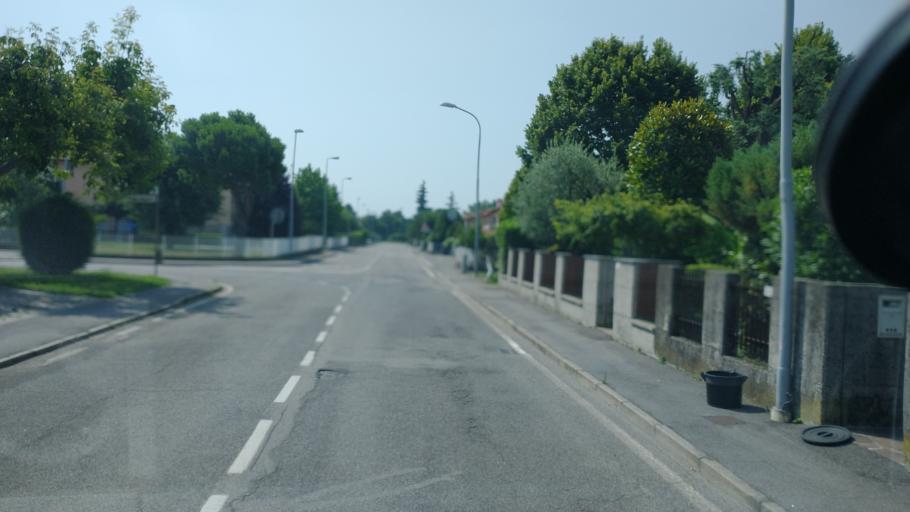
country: IT
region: Lombardy
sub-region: Provincia di Bergamo
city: Levate
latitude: 45.6258
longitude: 9.6183
